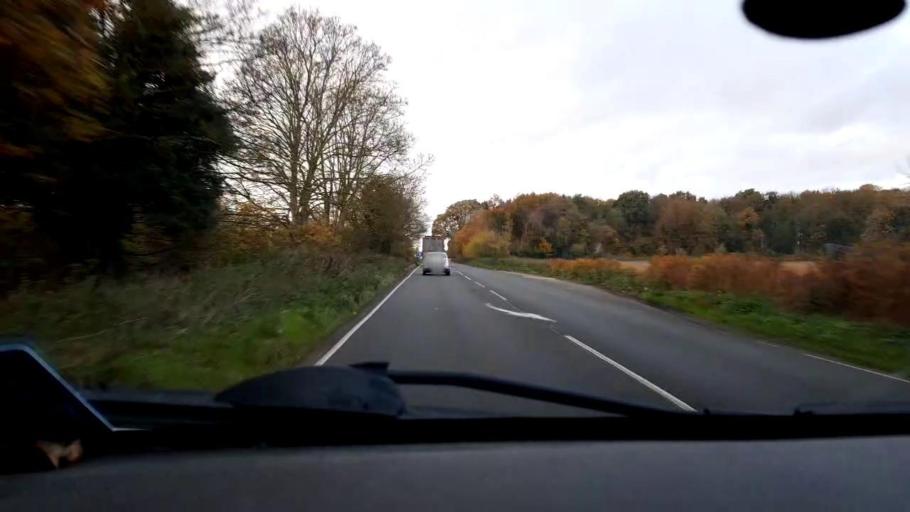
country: GB
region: England
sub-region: Norfolk
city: Costessey
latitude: 52.7006
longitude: 1.1601
